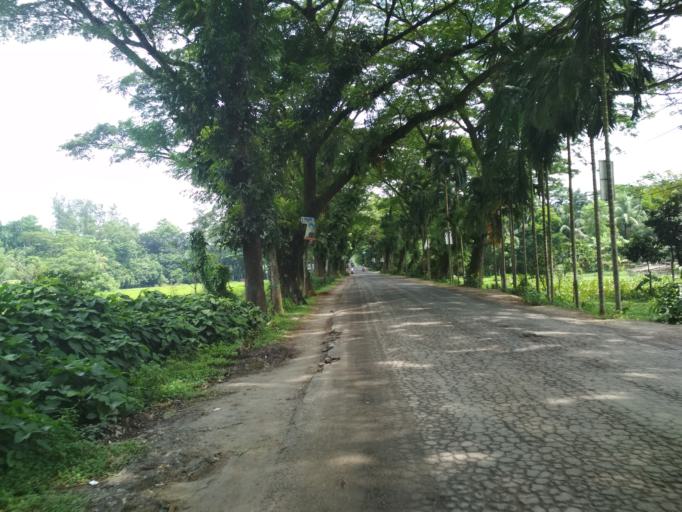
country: BD
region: Chittagong
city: Lakshmipur
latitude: 22.9502
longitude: 90.8087
